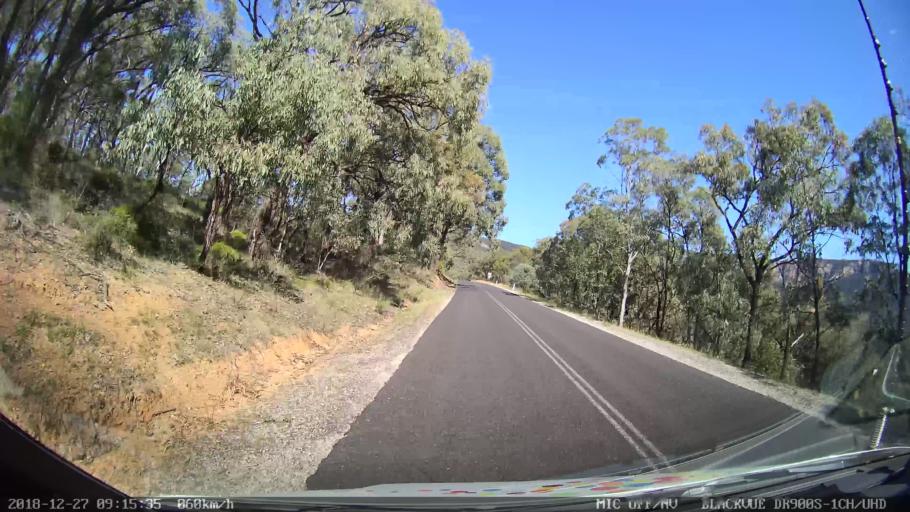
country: AU
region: New South Wales
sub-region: Lithgow
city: Portland
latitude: -33.1357
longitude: 150.0702
